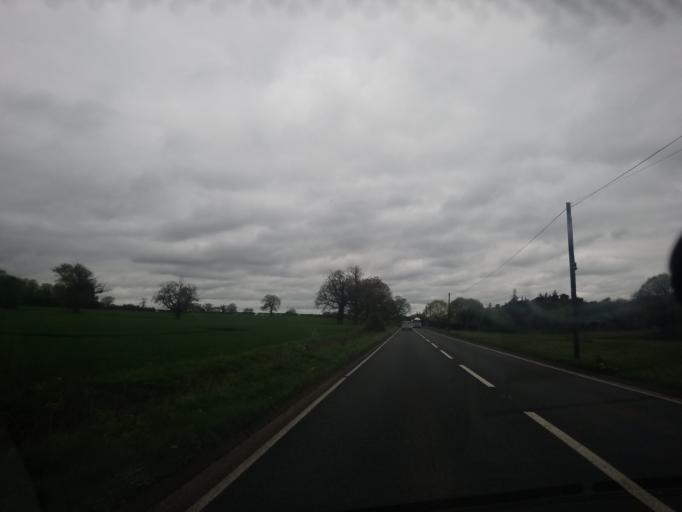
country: GB
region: England
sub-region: Telford and Wrekin
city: Chetwynd
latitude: 52.8015
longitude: -2.4263
